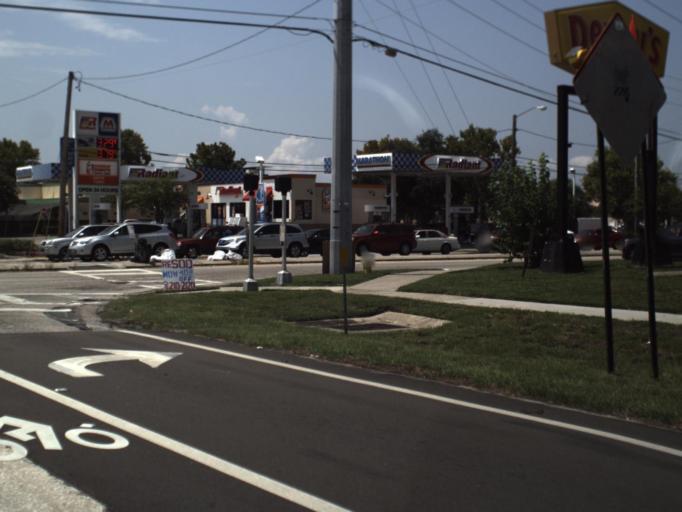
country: US
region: Florida
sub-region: Hillsborough County
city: Tampa
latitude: 27.9598
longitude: -82.5057
